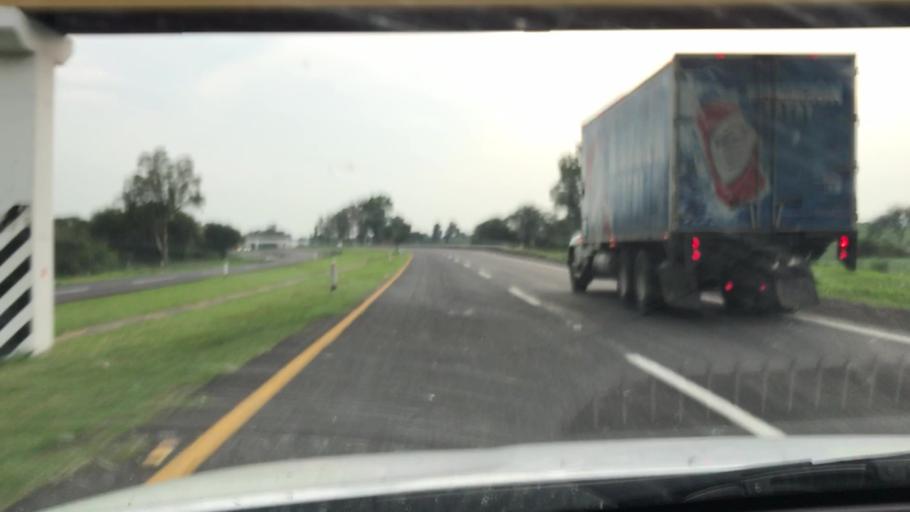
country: MX
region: Jalisco
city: La Barca
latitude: 20.3329
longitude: -102.5896
